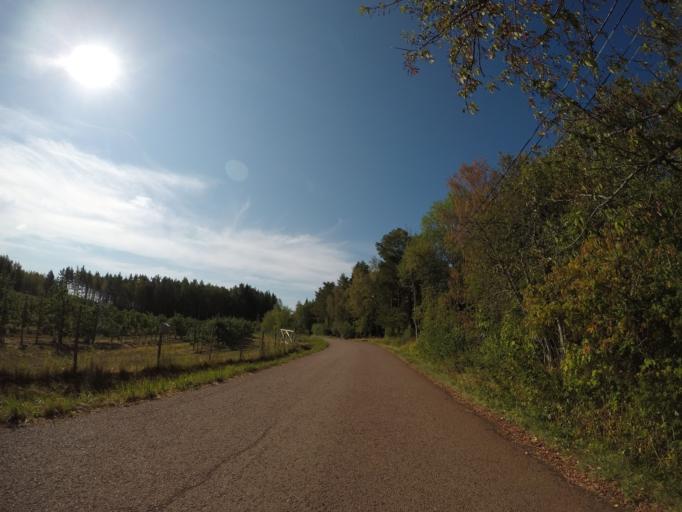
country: AX
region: Alands landsbygd
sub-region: Finstroem
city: Finstroem
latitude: 60.2785
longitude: 19.9172
